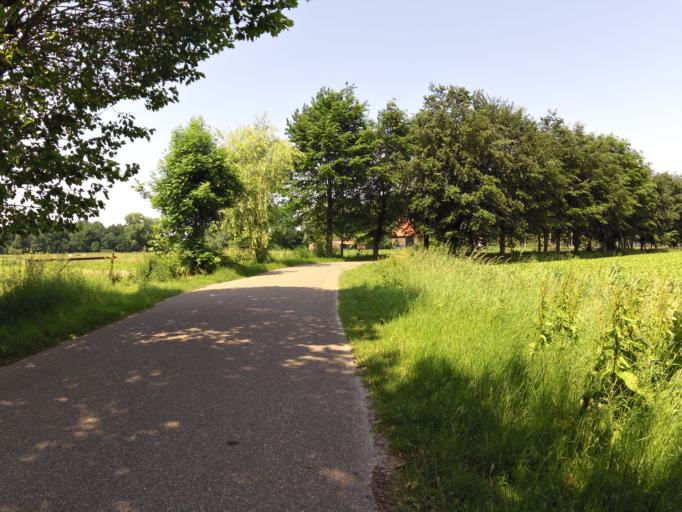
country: NL
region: North Brabant
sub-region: Gemeente Sint-Michielsgestel
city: Sint-Michielsgestel
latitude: 51.6264
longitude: 5.3544
